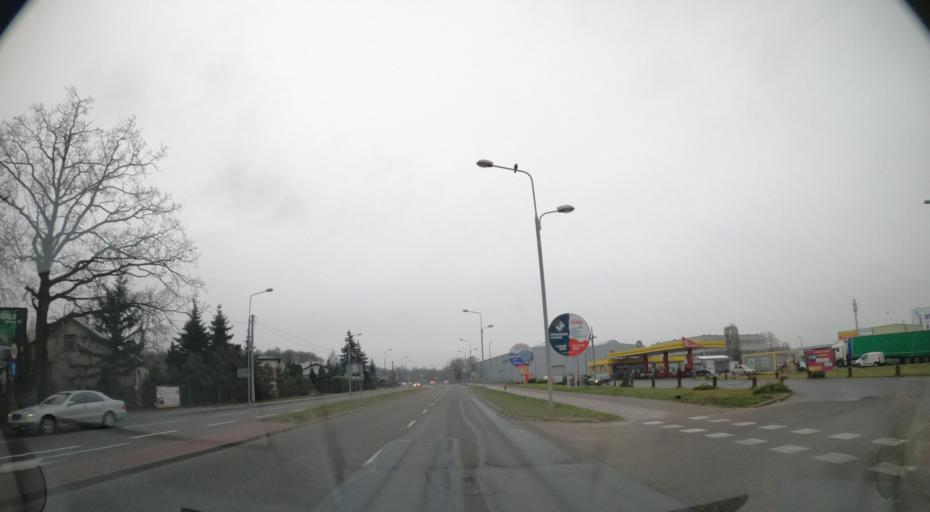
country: PL
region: Masovian Voivodeship
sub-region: Radom
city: Radom
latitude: 51.4170
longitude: 21.2051
